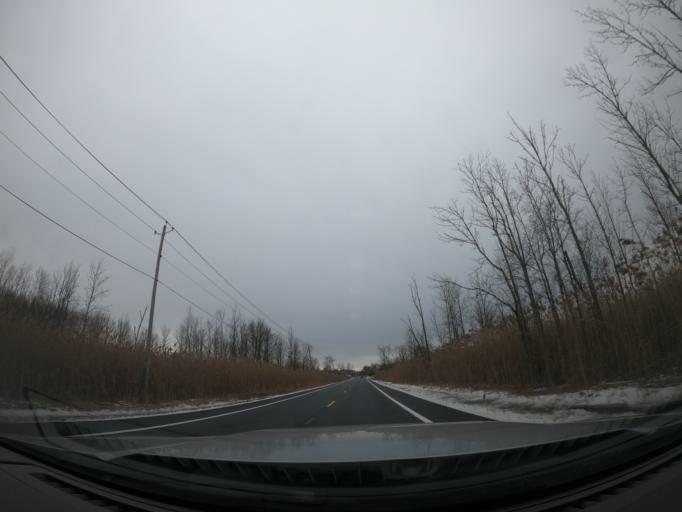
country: US
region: New York
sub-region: Madison County
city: Bridgeport
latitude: 43.1253
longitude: -75.9959
